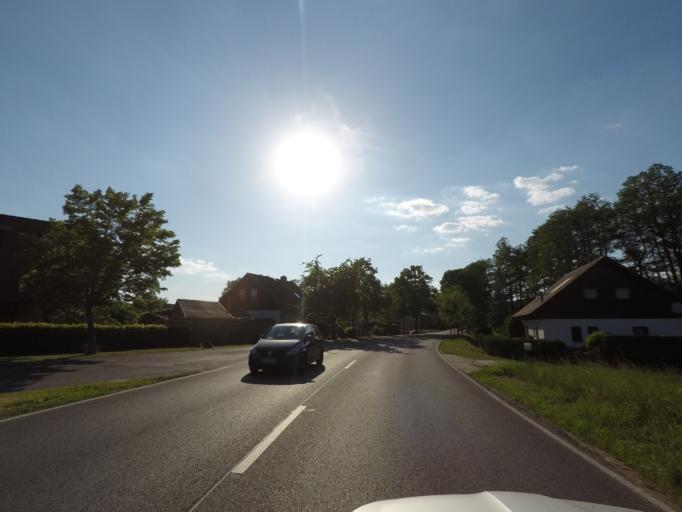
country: DE
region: Brandenburg
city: Hohenfinow
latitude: 52.8174
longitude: 13.8880
